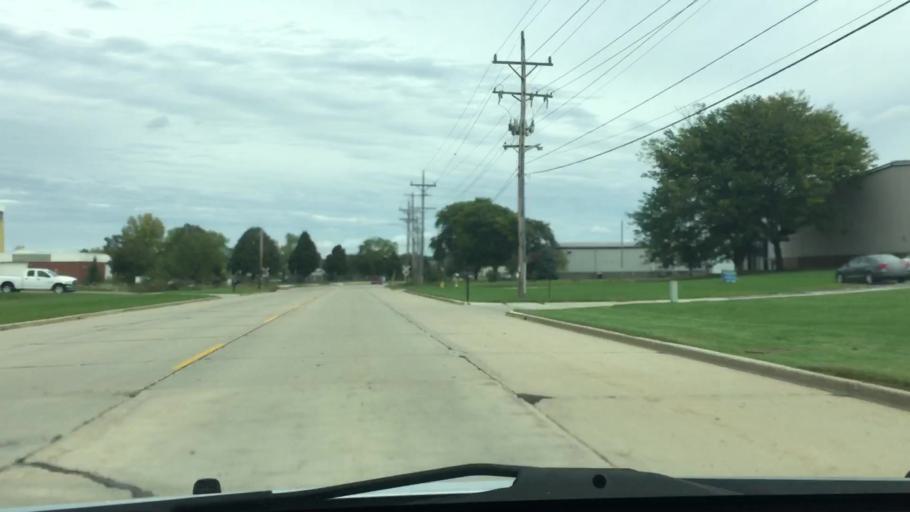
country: US
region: Wisconsin
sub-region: Waukesha County
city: Waukesha
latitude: 42.9925
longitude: -88.2497
